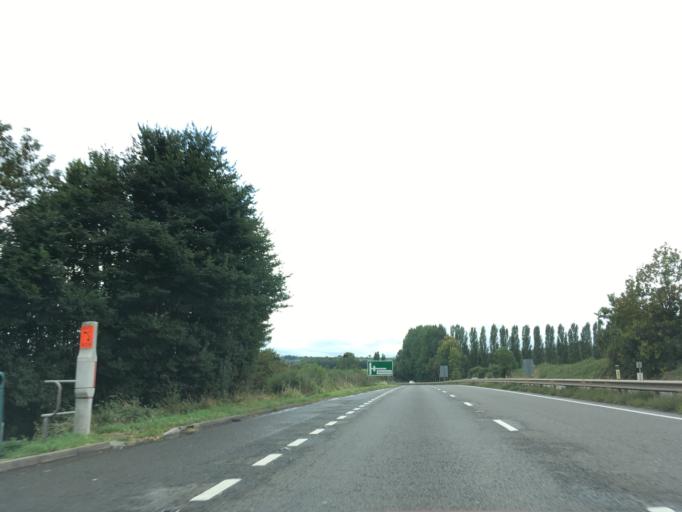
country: GB
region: England
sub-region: Herefordshire
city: Walford
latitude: 51.9081
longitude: -2.6201
